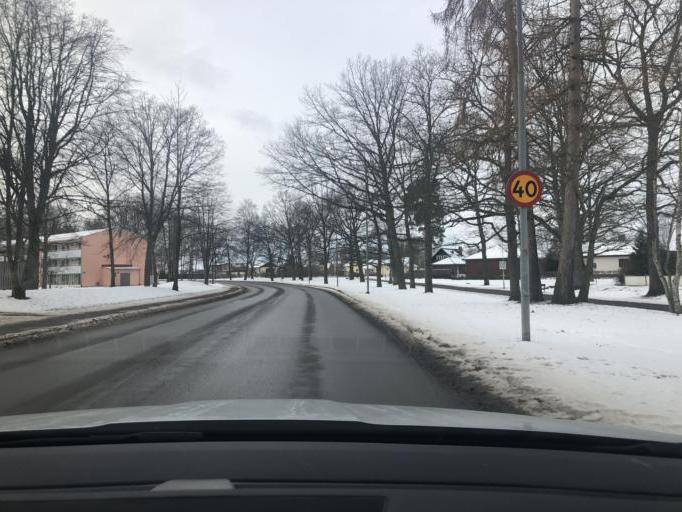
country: SE
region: OEstergoetland
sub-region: Motala Kommun
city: Motala
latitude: 58.5483
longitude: 15.0309
